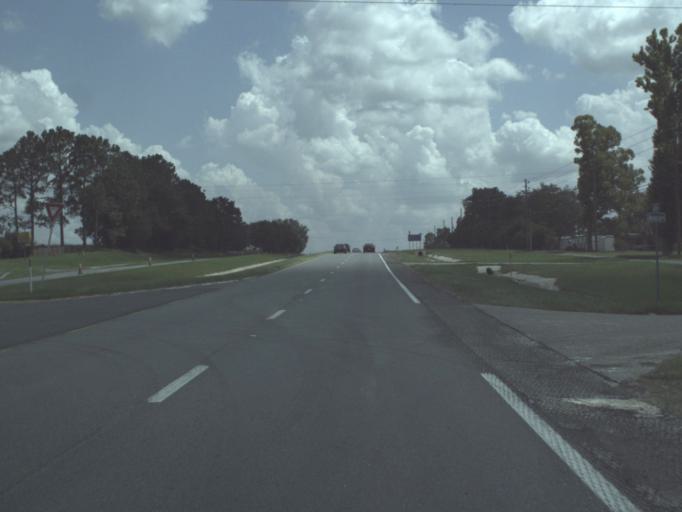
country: US
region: Florida
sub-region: Pasco County
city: Zephyrhills North
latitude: 28.2860
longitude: -82.1879
